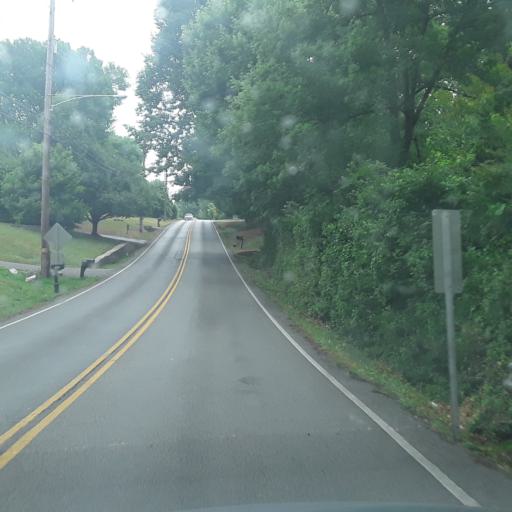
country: US
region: Tennessee
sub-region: Davidson County
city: Oak Hill
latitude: 36.0746
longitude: -86.7506
